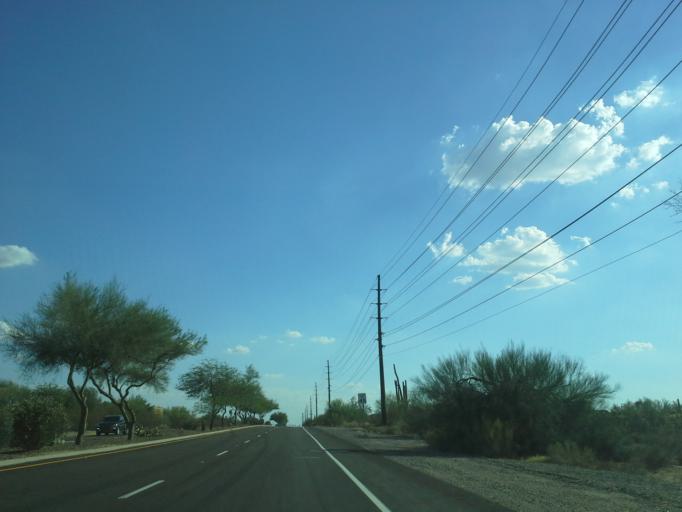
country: US
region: Arizona
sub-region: Maricopa County
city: Cave Creek
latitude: 33.8065
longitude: -111.9593
